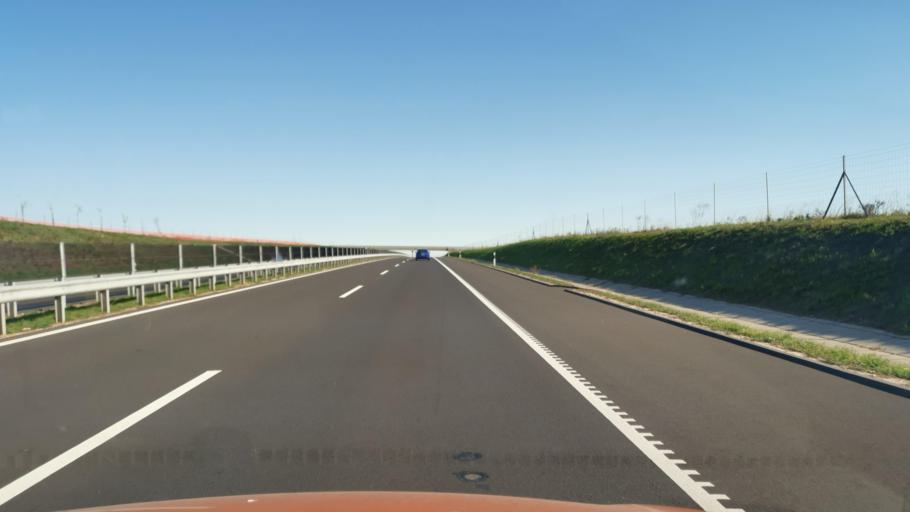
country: HU
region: Borsod-Abauj-Zemplen
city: Halmaj
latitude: 48.2747
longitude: 21.0030
